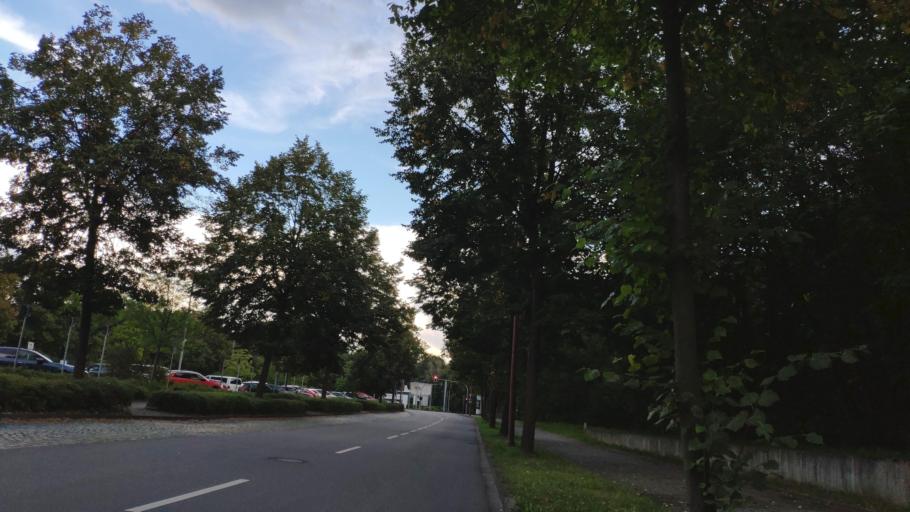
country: DE
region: Saxony
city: Chemnitz
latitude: 50.8033
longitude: 12.9043
